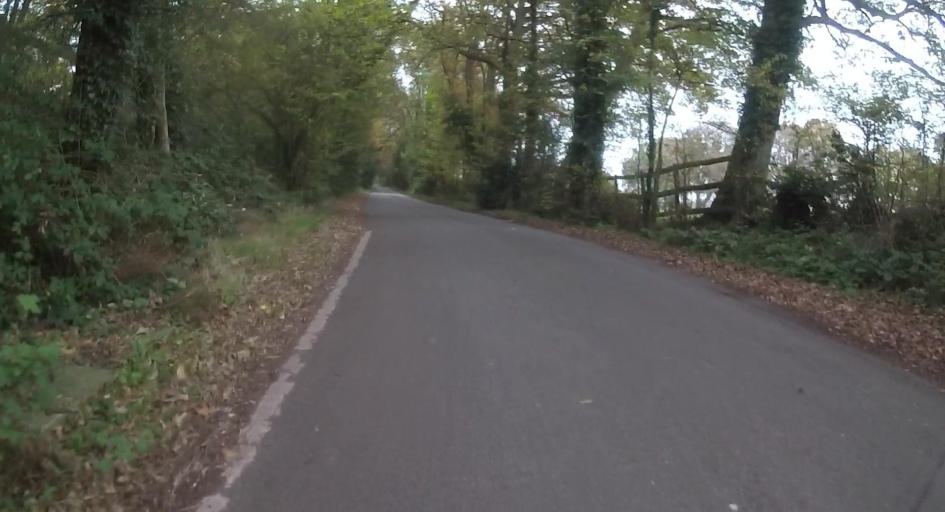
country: GB
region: England
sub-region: Hampshire
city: Eversley
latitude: 51.3737
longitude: -0.8776
